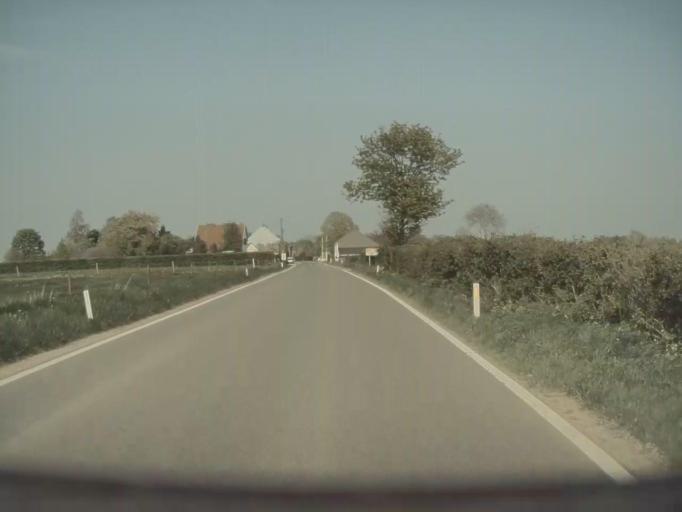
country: BE
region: Wallonia
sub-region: Province de Namur
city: Somme-Leuze
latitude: 50.3498
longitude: 5.3030
